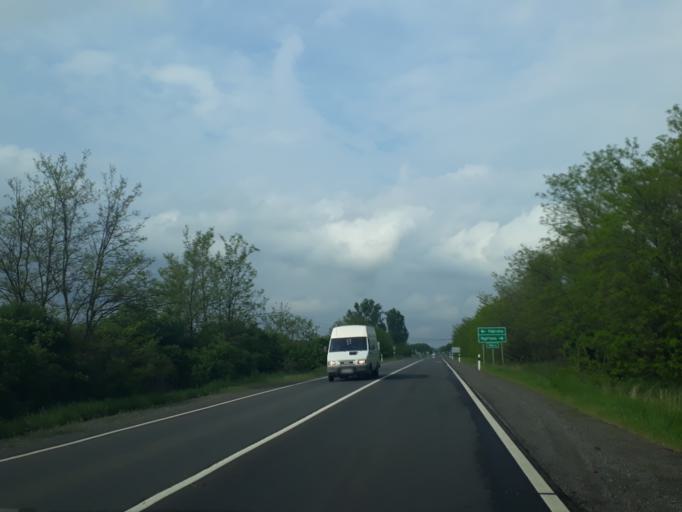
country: HU
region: Szabolcs-Szatmar-Bereg
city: Nyirtass
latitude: 48.1228
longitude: 22.0071
